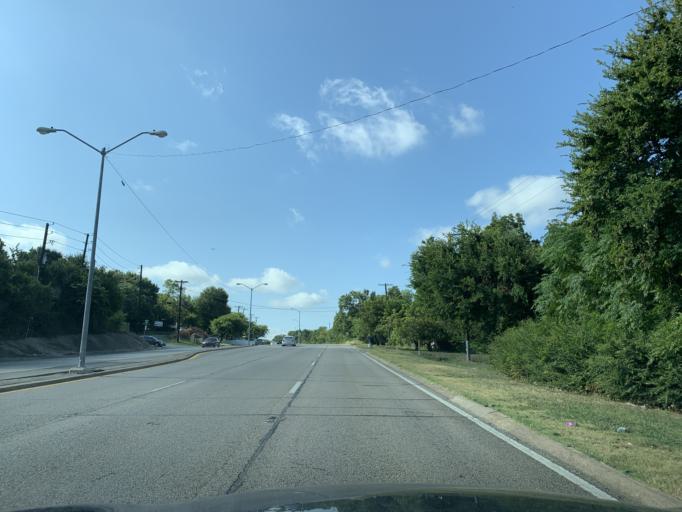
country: US
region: Texas
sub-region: Dallas County
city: Hutchins
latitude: 32.6768
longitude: -96.7852
